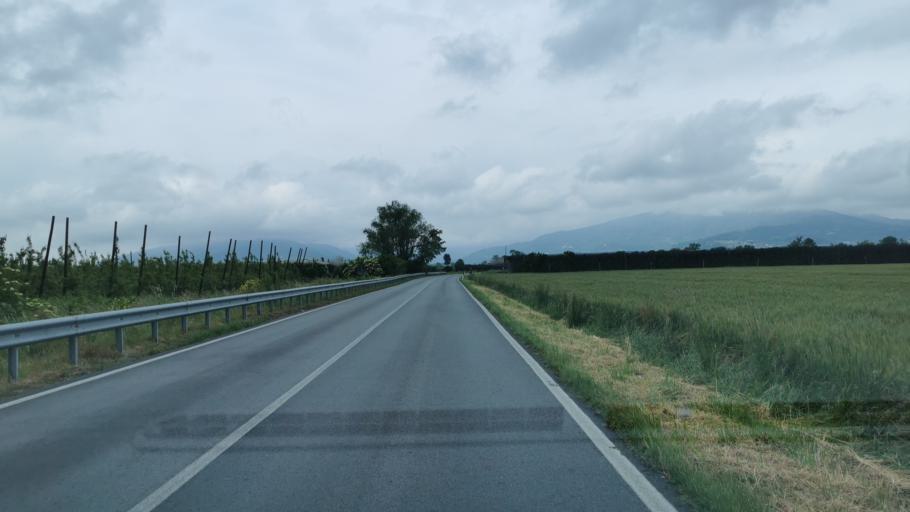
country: IT
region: Piedmont
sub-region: Provincia di Cuneo
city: Villafalletto
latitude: 44.5863
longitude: 7.5407
